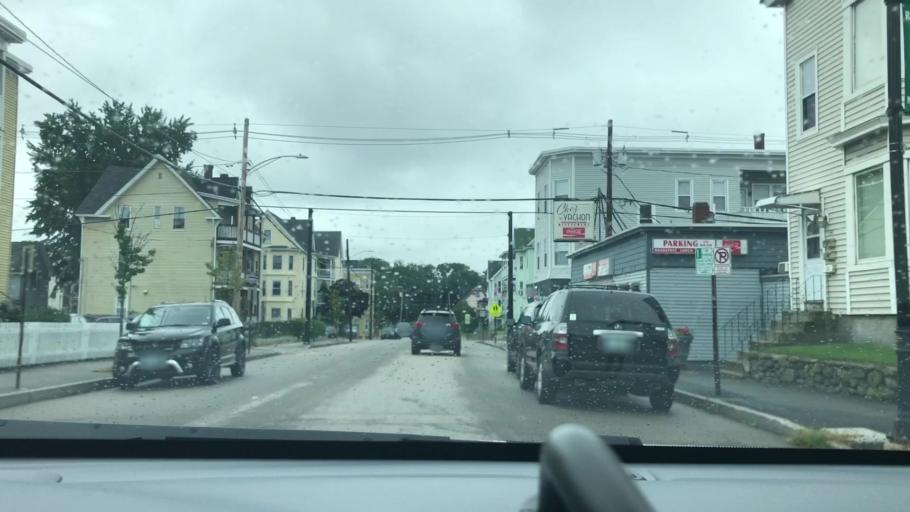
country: US
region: New Hampshire
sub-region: Hillsborough County
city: Manchester
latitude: 42.9953
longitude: -71.4787
